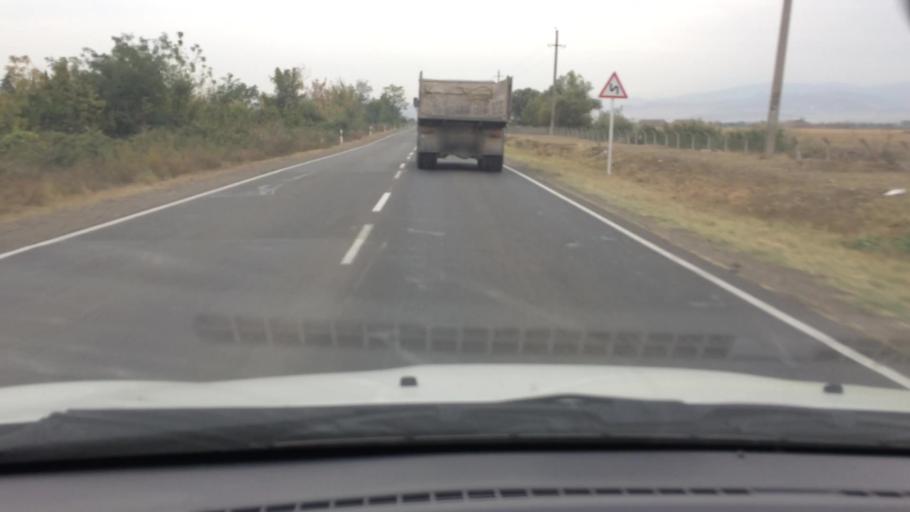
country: GE
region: Kvemo Kartli
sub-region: Marneuli
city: Marneuli
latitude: 41.4685
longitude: 44.8046
